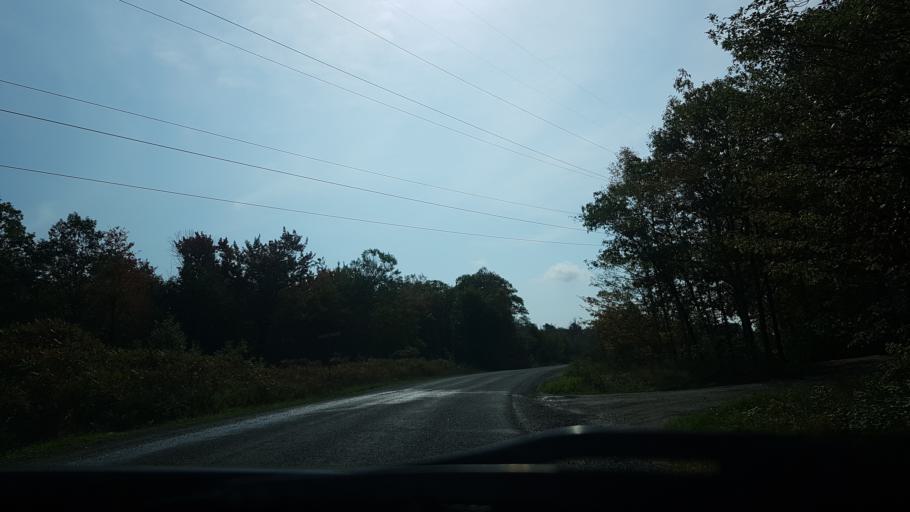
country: CA
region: Ontario
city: Gravenhurst
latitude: 44.8270
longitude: -79.2133
